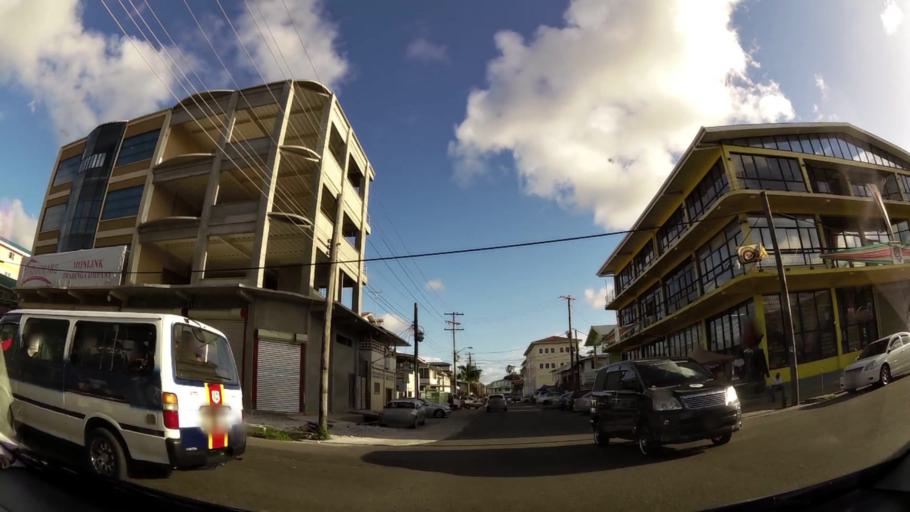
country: GY
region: Demerara-Mahaica
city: Georgetown
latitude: 6.8084
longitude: -58.1537
